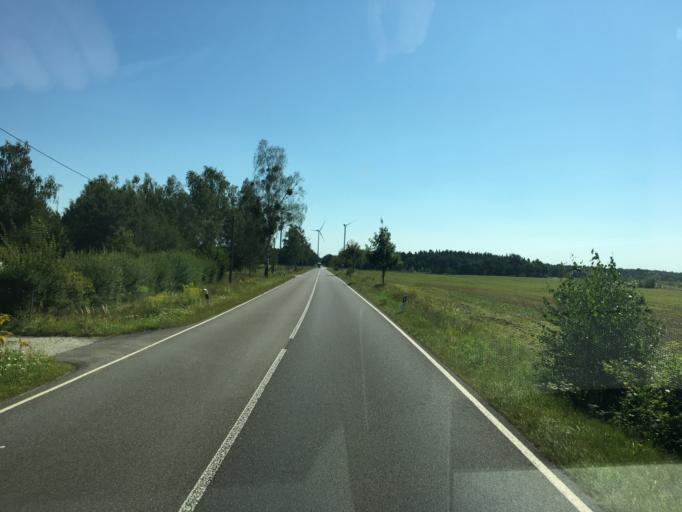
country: DE
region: Brandenburg
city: Welzow
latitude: 51.5549
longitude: 14.1409
